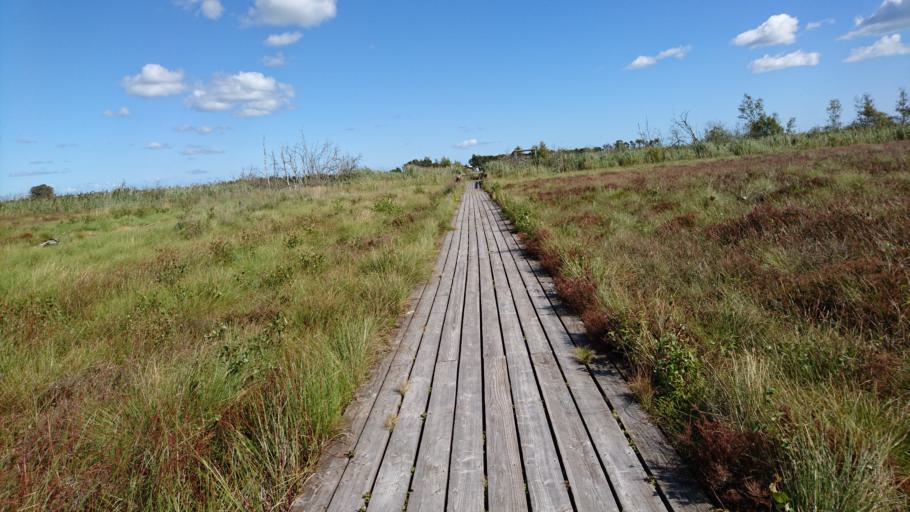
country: DK
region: North Denmark
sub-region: Alborg Kommune
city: Storvorde
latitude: 56.9106
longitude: 10.1834
